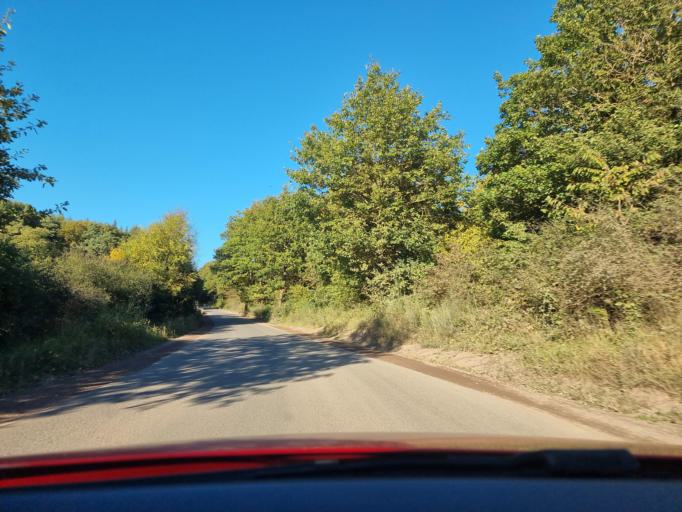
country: DE
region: Rheinland-Pfalz
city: Neumagen-Dhron
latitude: 49.8746
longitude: 6.8861
